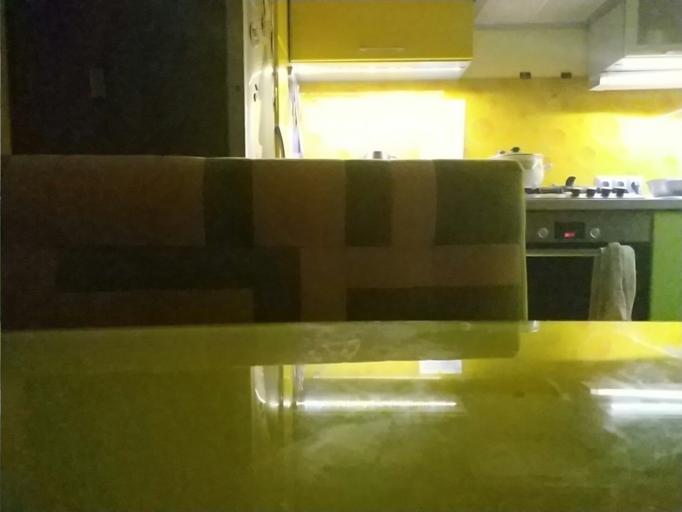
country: RU
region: Republic of Karelia
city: Pyaozerskiy
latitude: 65.4613
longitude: 30.6278
